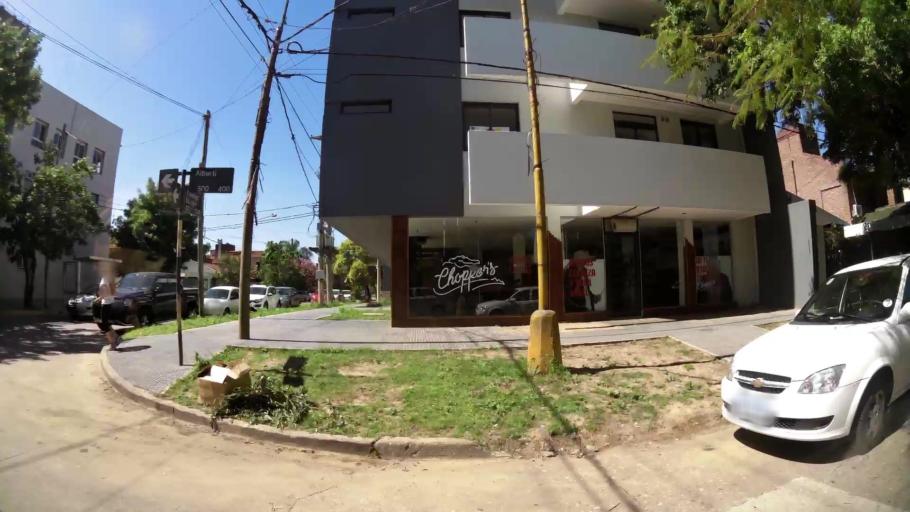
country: AR
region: Santa Fe
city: Santa Fe de la Vera Cruz
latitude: -31.6067
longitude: -60.6707
